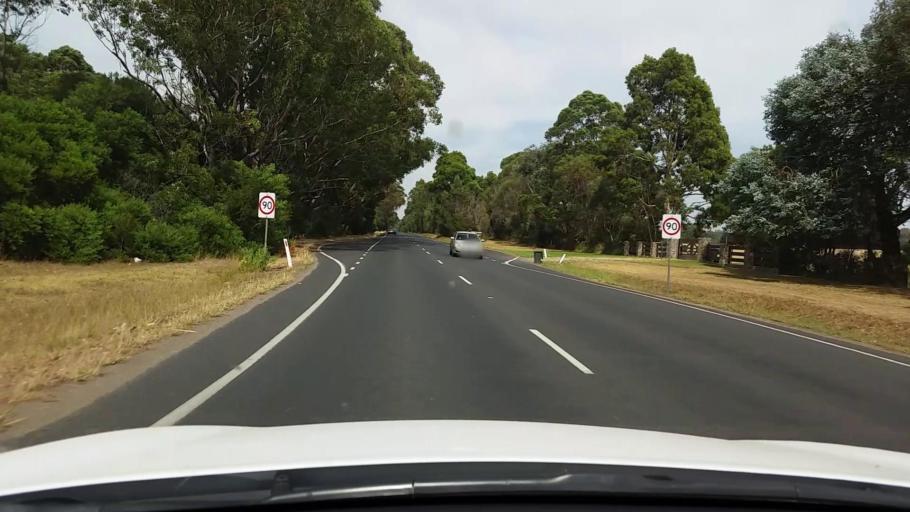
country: AU
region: Victoria
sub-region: Mornington Peninsula
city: Balnarring
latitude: -38.3612
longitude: 145.1447
